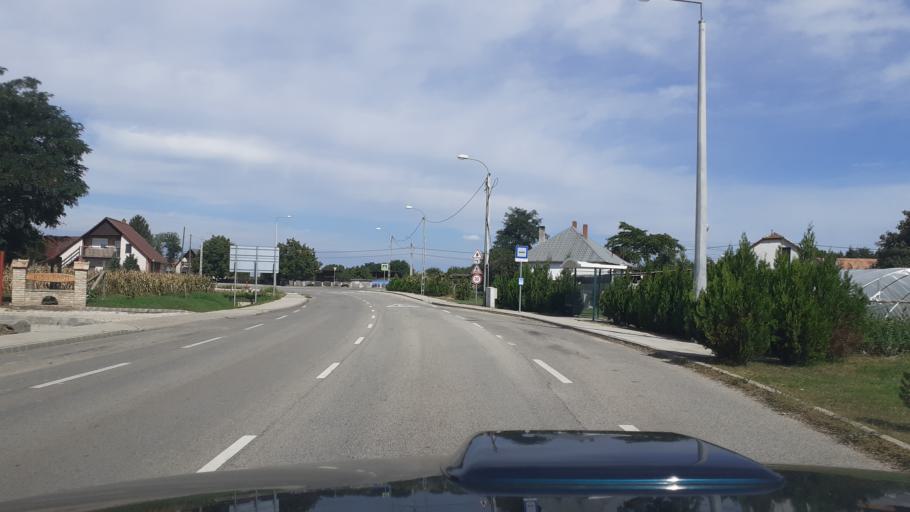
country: HU
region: Fejer
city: Seregelyes
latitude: 47.1067
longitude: 18.6281
